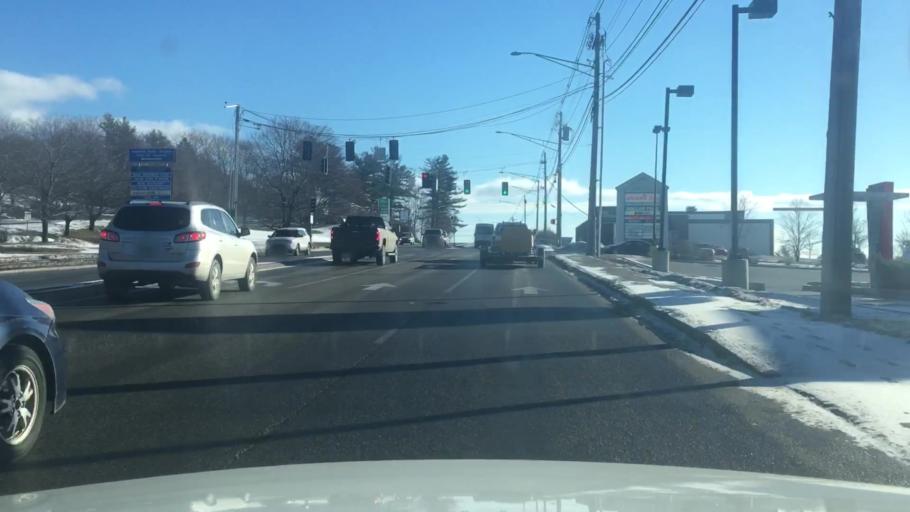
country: US
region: Maine
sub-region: Kennebec County
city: Augusta
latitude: 44.3132
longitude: -69.7955
